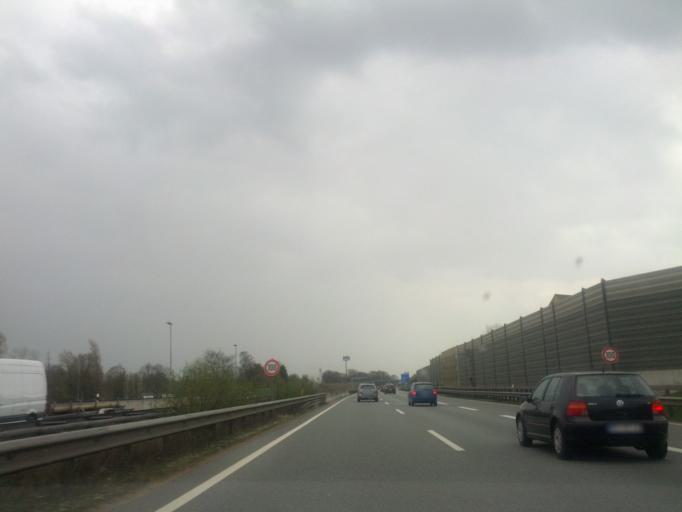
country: DE
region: Lower Saxony
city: Stuhr
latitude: 53.0196
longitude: 8.6905
